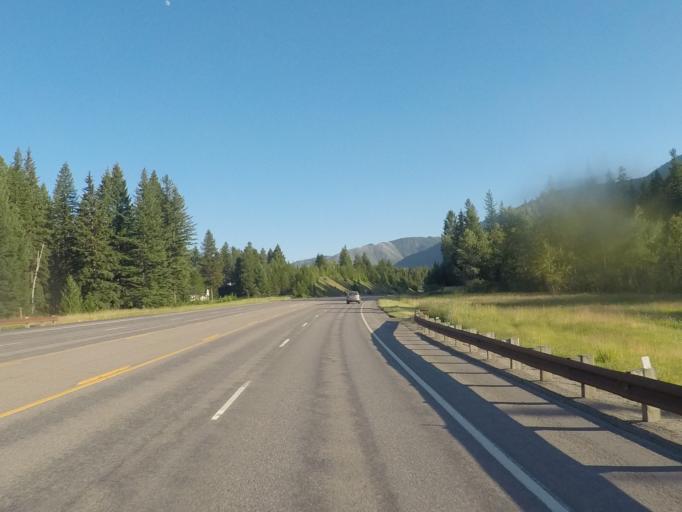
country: US
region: Montana
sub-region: Flathead County
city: Columbia Falls
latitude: 48.3949
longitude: -114.0408
